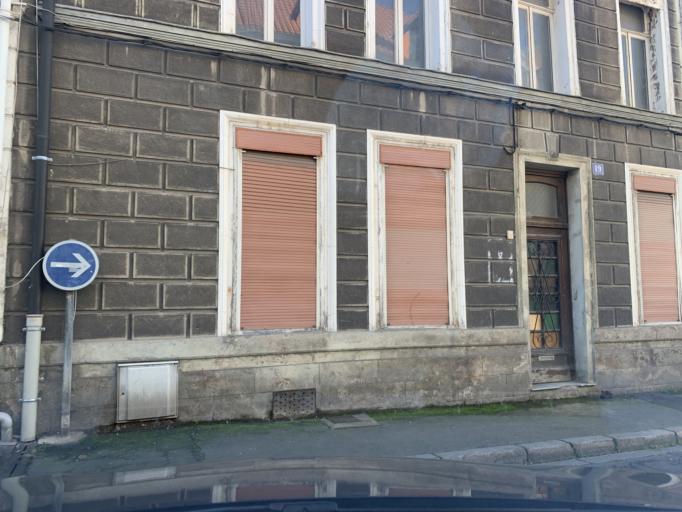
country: FR
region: Nord-Pas-de-Calais
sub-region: Departement du Nord
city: Cambrai
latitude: 50.1787
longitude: 3.2338
